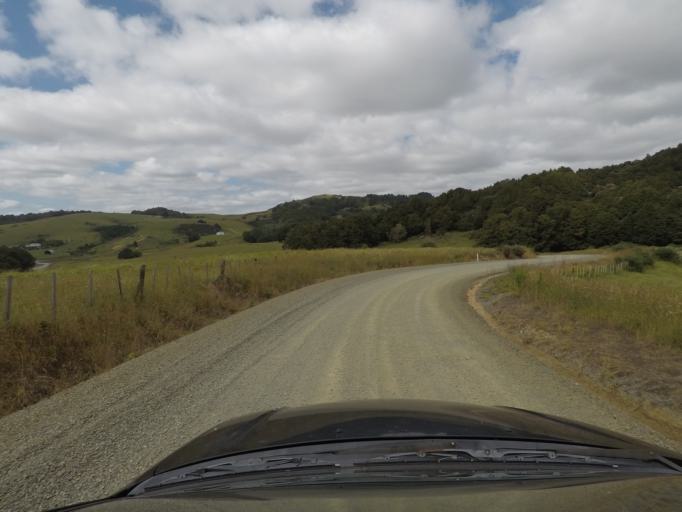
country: NZ
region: Northland
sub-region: Whangarei
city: Ruakaka
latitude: -35.9311
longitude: 174.3461
